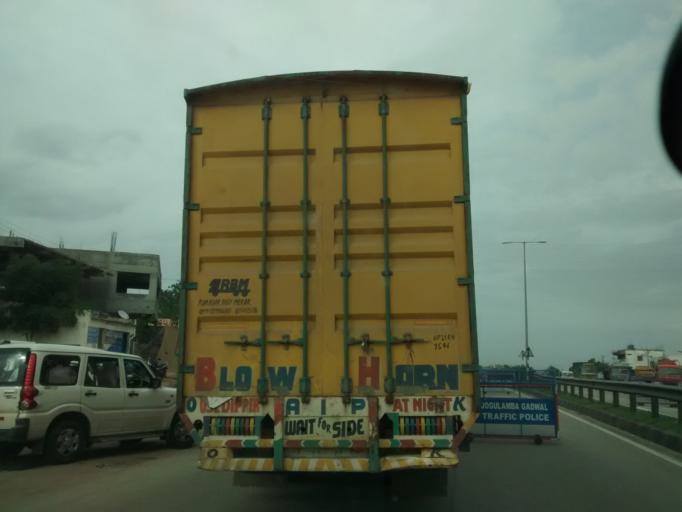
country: IN
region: Telangana
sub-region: Mahbubnagar
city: Gadwal
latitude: 16.1472
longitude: 77.9070
